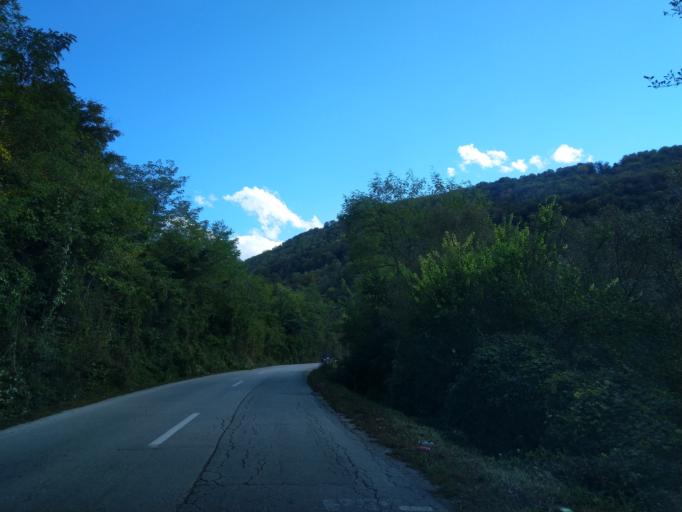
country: RS
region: Central Serbia
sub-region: Zlatiborski Okrug
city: Uzice
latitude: 43.8814
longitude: 19.7785
